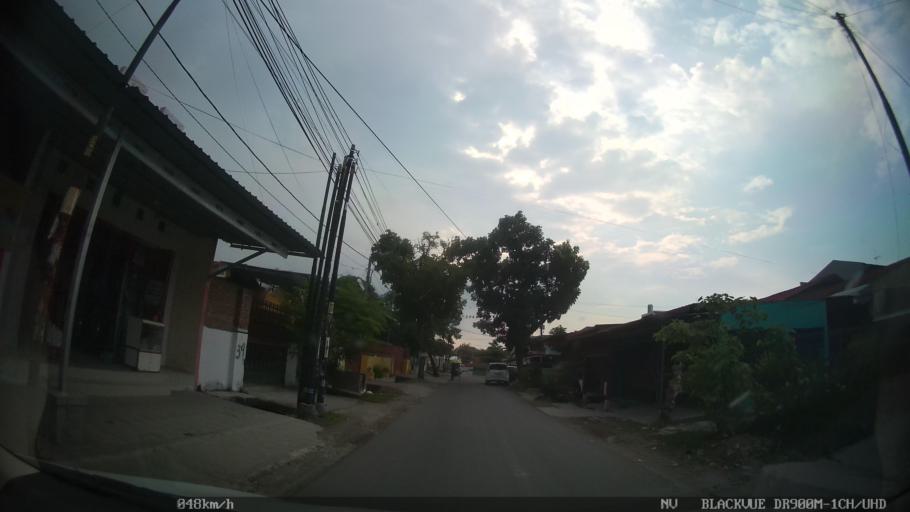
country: ID
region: North Sumatra
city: Medan
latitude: 3.6074
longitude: 98.6979
